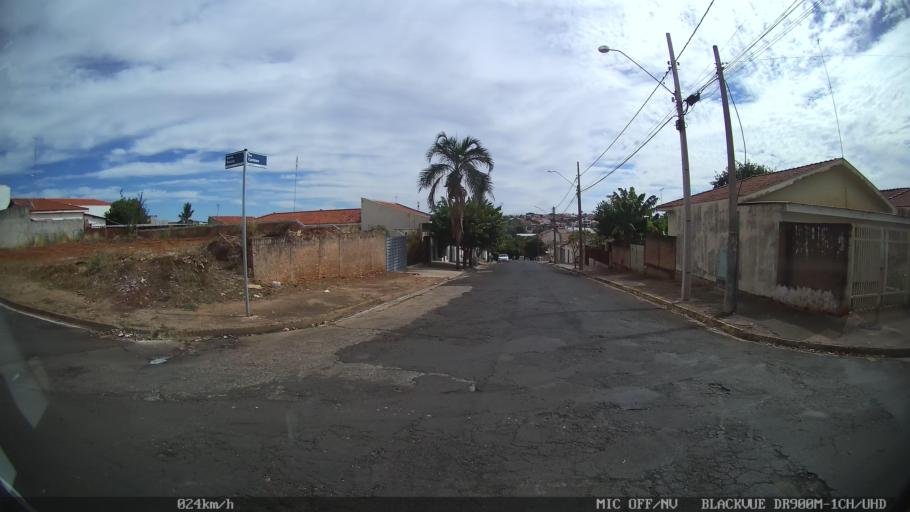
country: BR
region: Sao Paulo
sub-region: Catanduva
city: Catanduva
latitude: -21.1555
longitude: -48.9764
